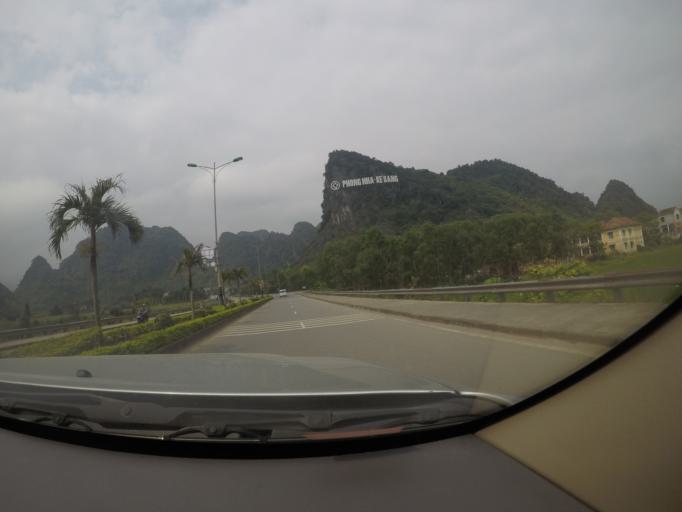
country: VN
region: Quang Binh
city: Ba Don
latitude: 17.6106
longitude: 106.3181
